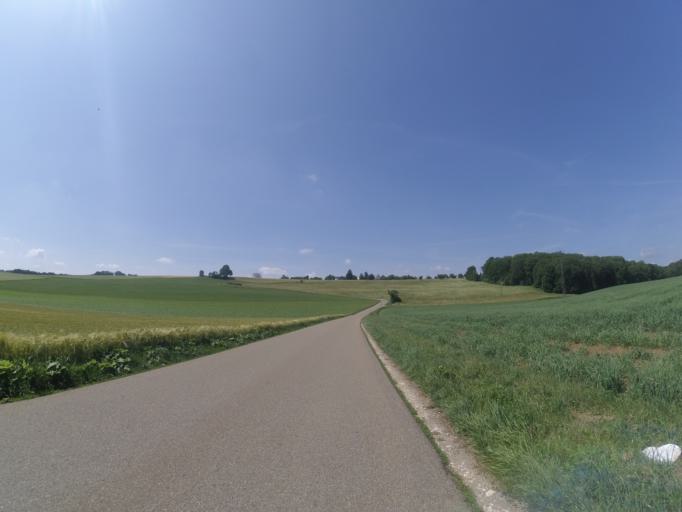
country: DE
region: Baden-Wuerttemberg
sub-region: Tuebingen Region
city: Bernstadt
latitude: 48.4787
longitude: 10.0221
